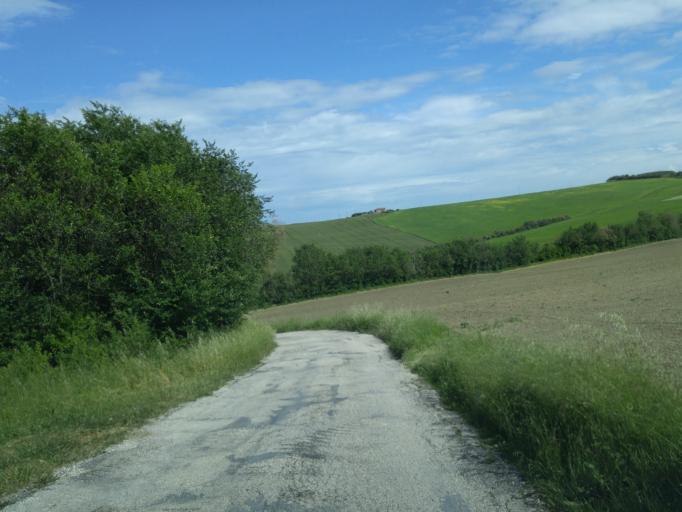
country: IT
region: The Marches
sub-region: Provincia di Pesaro e Urbino
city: San Costanzo
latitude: 43.7976
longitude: 13.0537
